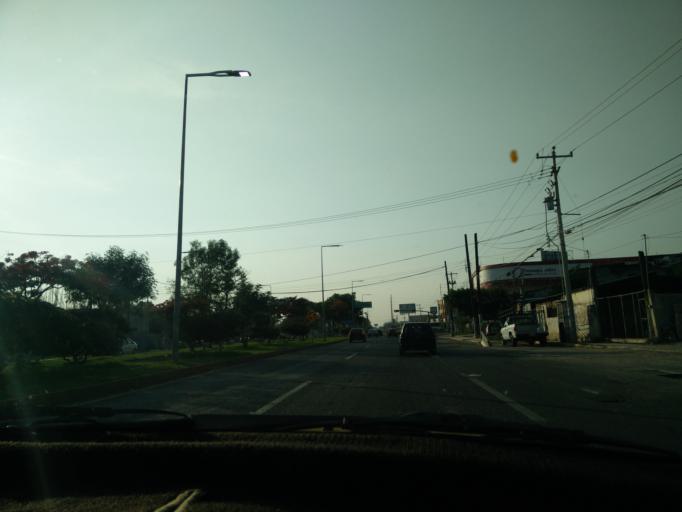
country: MX
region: Oaxaca
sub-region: Santa Maria Atzompa
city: San Jeronimo Yahuiche
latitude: 17.1214
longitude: -96.7633
